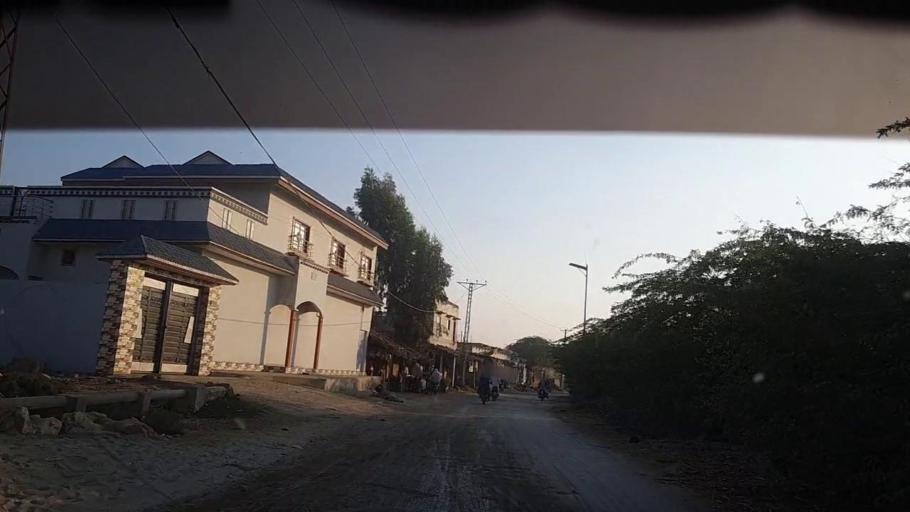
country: PK
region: Sindh
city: Ranipur
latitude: 27.2804
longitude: 68.5156
